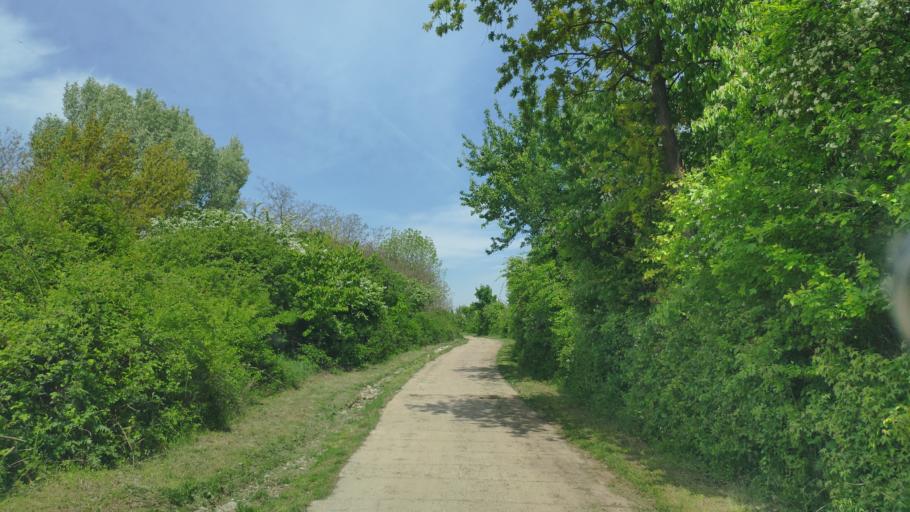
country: SK
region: Kosicky
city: Secovce
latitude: 48.6862
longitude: 21.6071
